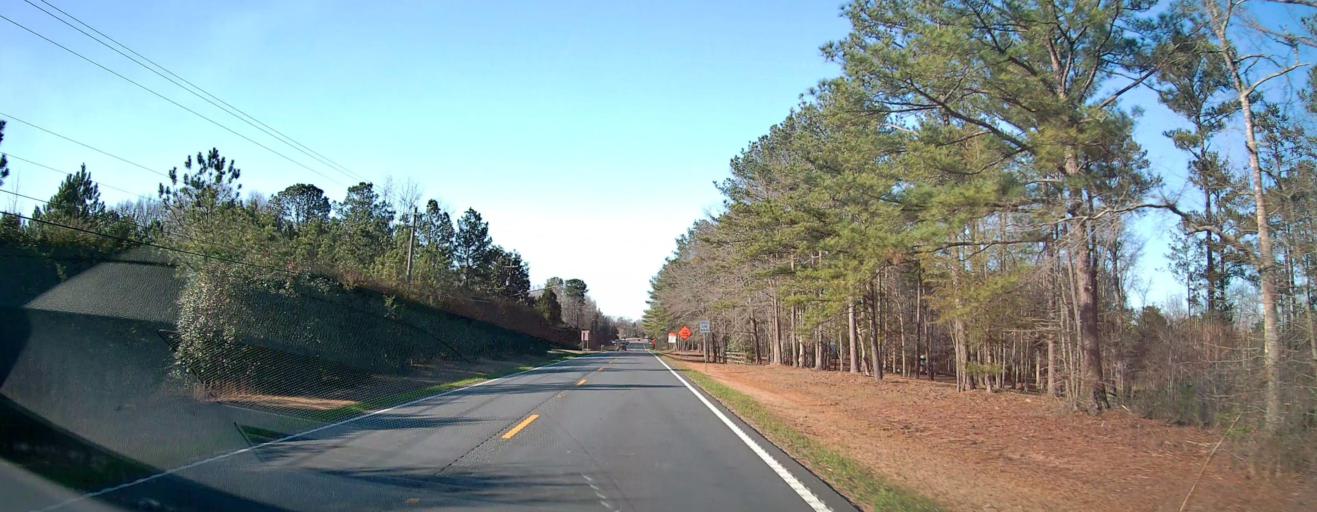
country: US
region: Georgia
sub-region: Talbot County
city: Sardis
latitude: 32.8013
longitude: -84.6943
